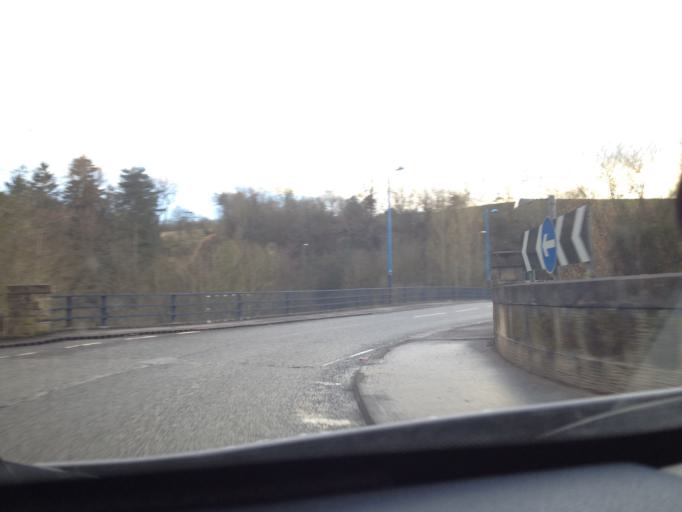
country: GB
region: Scotland
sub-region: South Lanarkshire
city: Dalserf
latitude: 55.7374
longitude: -3.9220
